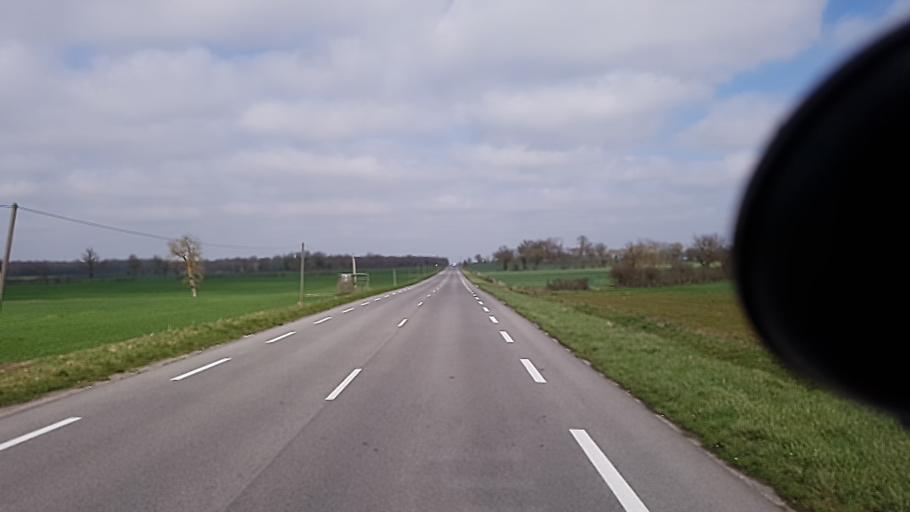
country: FR
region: Rhone-Alpes
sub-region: Departement de l'Ain
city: Villars-les-Dombes
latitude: 46.0209
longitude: 5.0556
